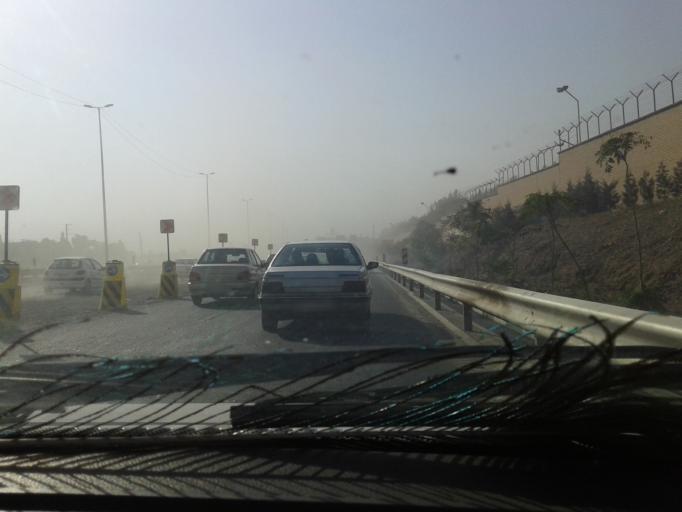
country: IR
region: Tehran
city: Tehran
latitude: 35.7232
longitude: 51.6085
